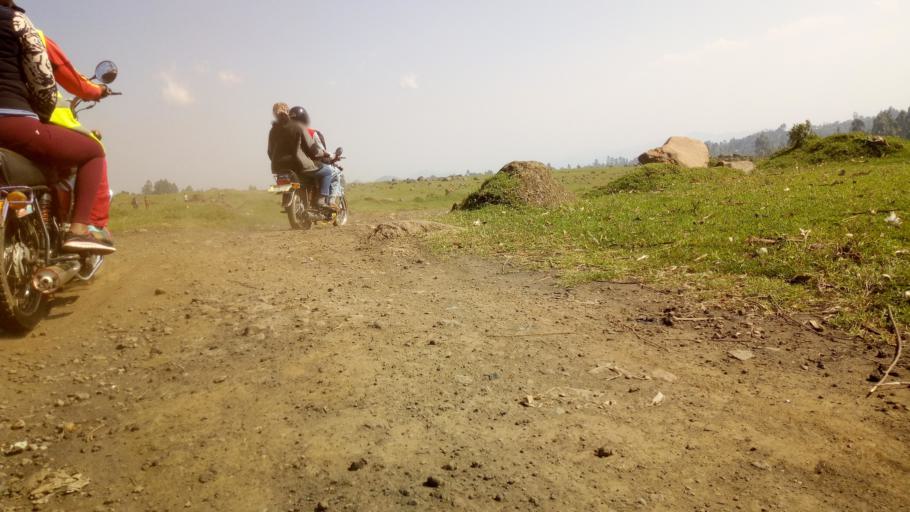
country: UG
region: Western Region
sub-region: Kisoro District
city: Kisoro
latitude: -1.3417
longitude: 29.6284
